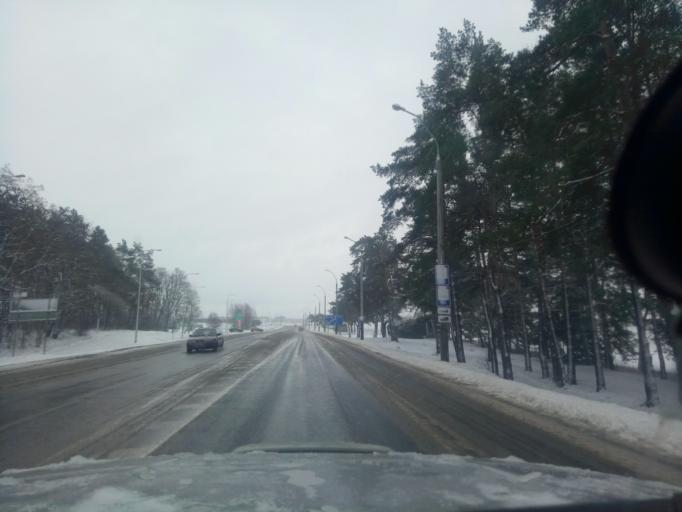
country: BY
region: Minsk
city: Nyasvizh
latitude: 53.2427
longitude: 26.6292
